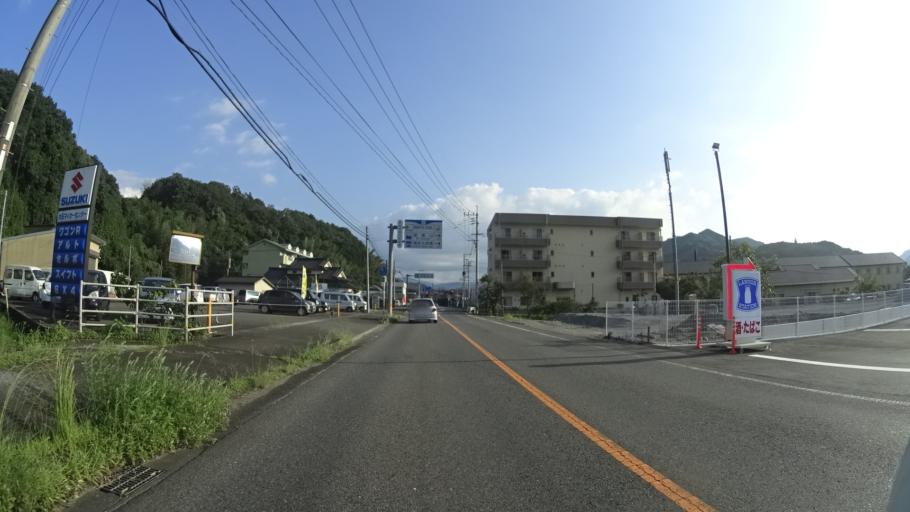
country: JP
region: Oita
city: Bungo-Takada-shi
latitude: 33.4549
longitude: 131.3289
